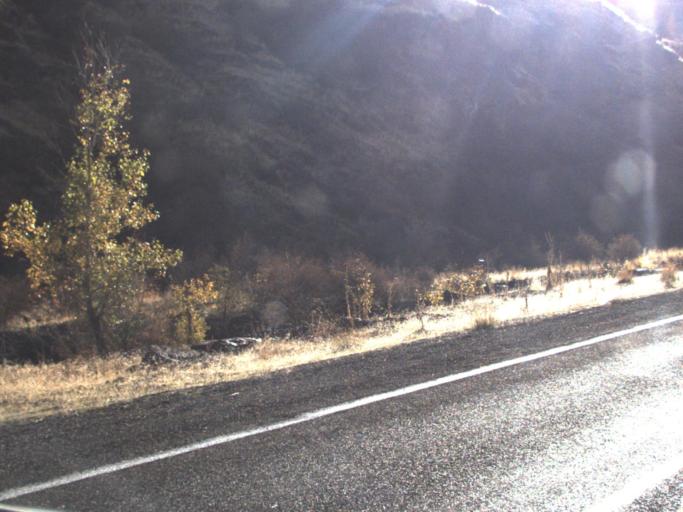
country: US
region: Washington
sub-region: Asotin County
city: Asotin
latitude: 46.0277
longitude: -117.2574
